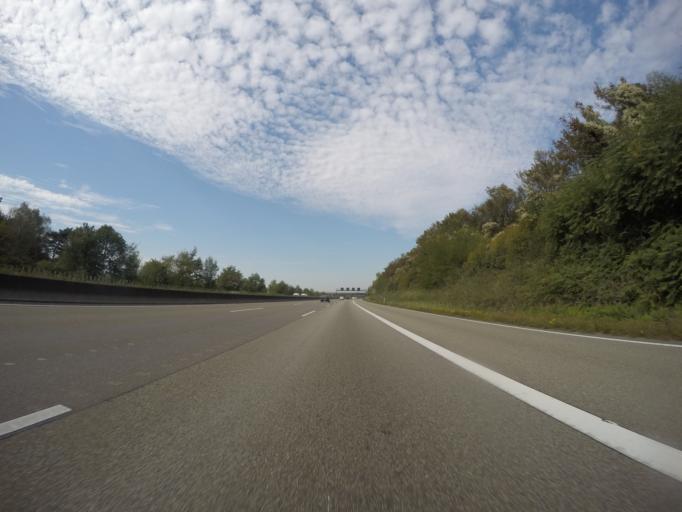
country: DE
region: Hesse
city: Obertshausen
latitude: 50.0626
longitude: 8.8459
